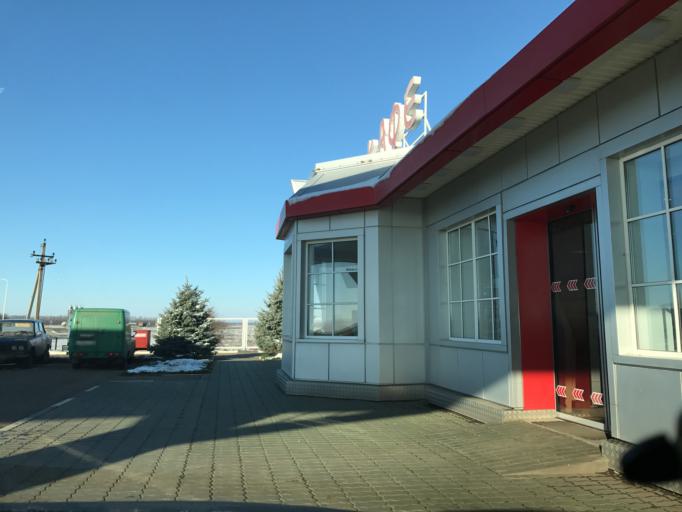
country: RU
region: Rostov
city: Peschanokopskoye
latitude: 46.2745
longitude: 40.9632
